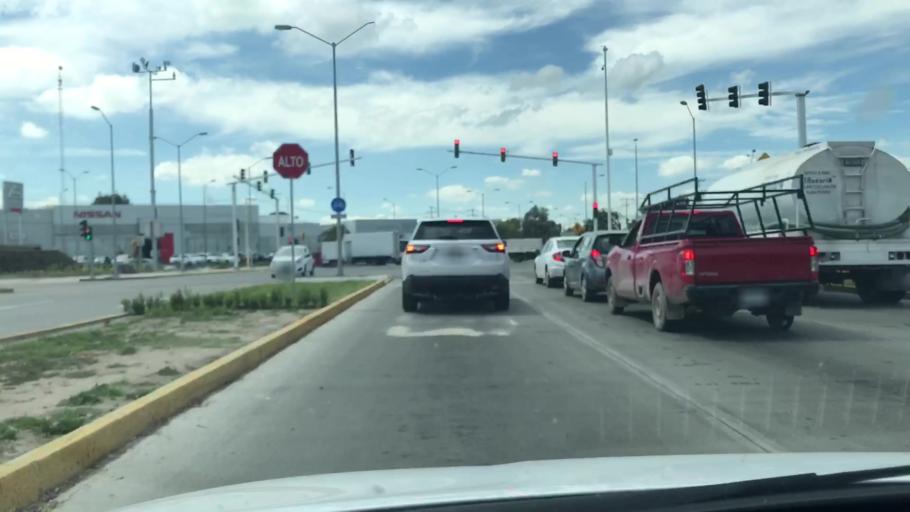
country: MX
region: Guanajuato
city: Celaya
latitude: 20.5161
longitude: -100.7800
